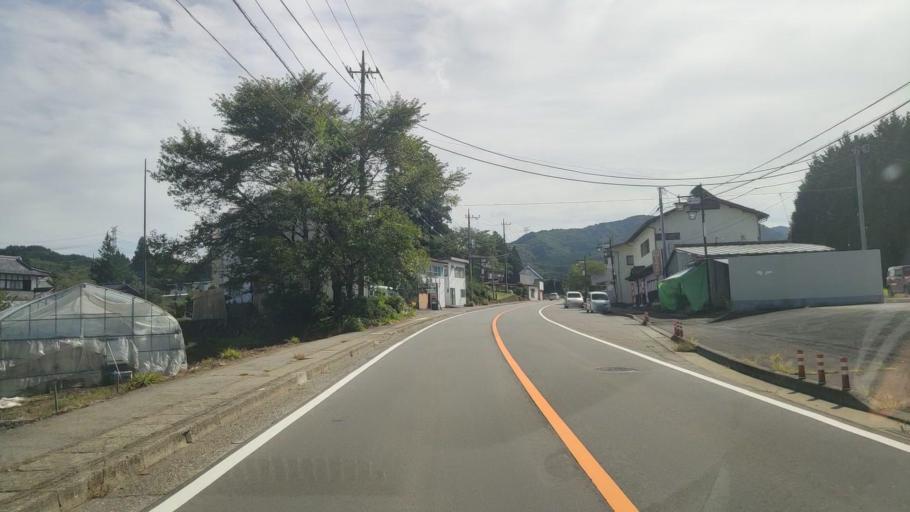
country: JP
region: Gunma
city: Numata
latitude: 36.6285
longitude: 138.9617
